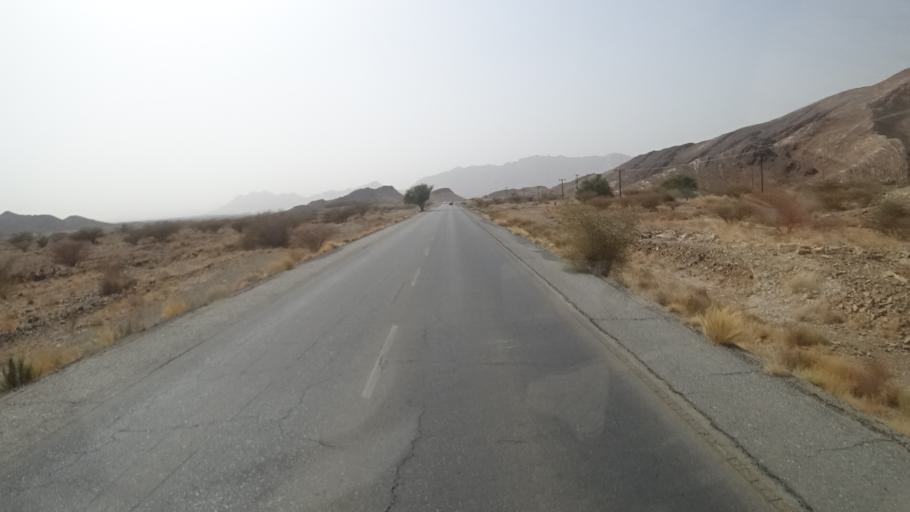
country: OM
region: Muhafazat ad Dakhiliyah
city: Nizwa
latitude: 22.9253
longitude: 57.6397
